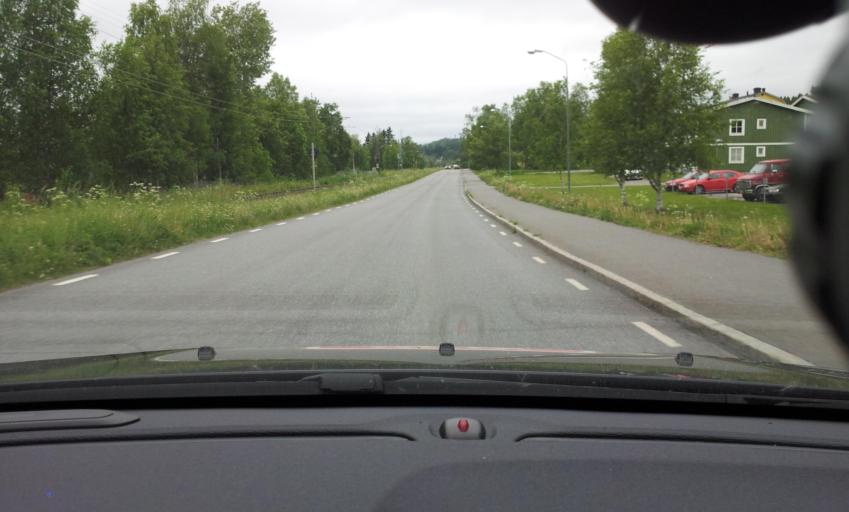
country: SE
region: Jaemtland
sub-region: Are Kommun
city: Jarpen
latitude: 63.3064
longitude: 13.6737
